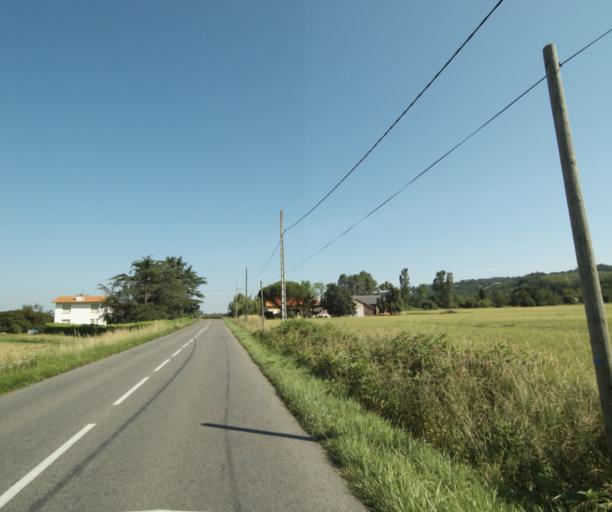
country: FR
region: Midi-Pyrenees
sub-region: Departement du Tarn-et-Garonne
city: Corbarieu
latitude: 43.9566
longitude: 1.3636
